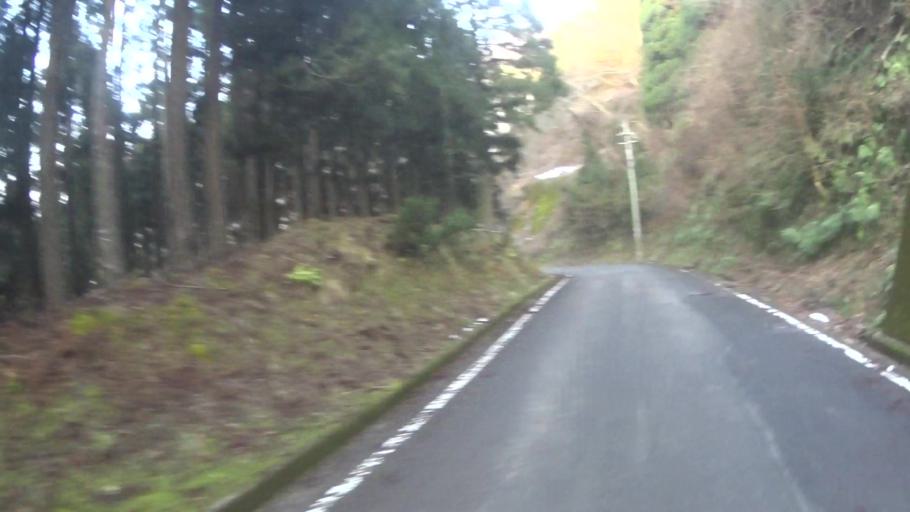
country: JP
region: Kyoto
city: Maizuru
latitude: 35.3582
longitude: 135.4674
